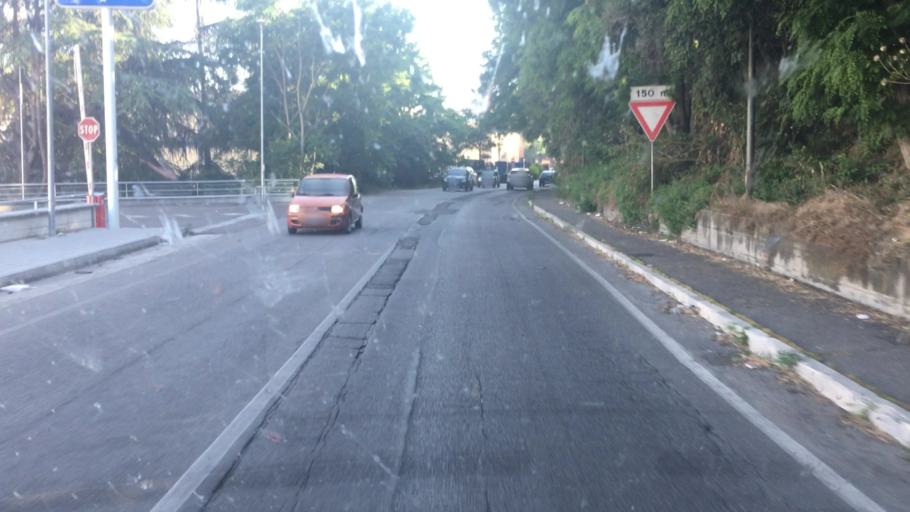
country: IT
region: Basilicate
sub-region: Provincia di Potenza
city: Potenza
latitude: 40.6314
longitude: 15.8108
